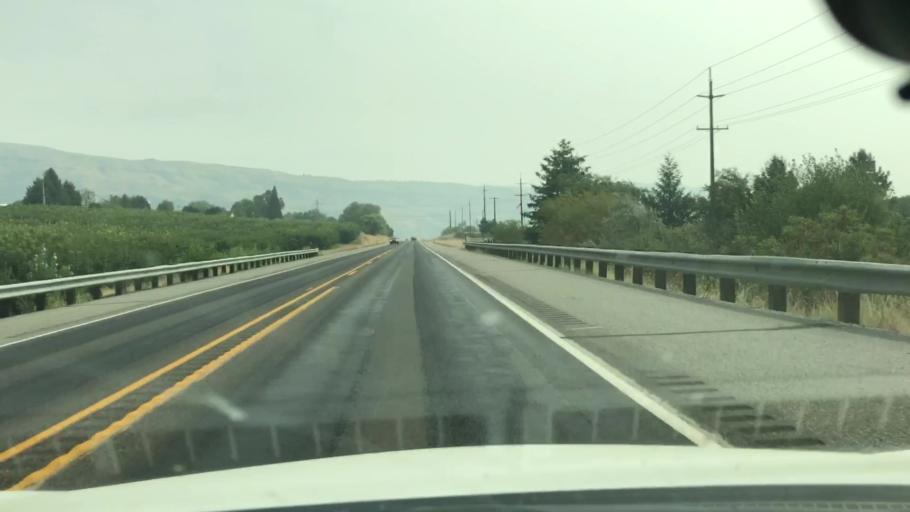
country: US
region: Washington
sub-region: Chelan County
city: South Wenatchee
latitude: 47.3723
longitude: -120.1623
